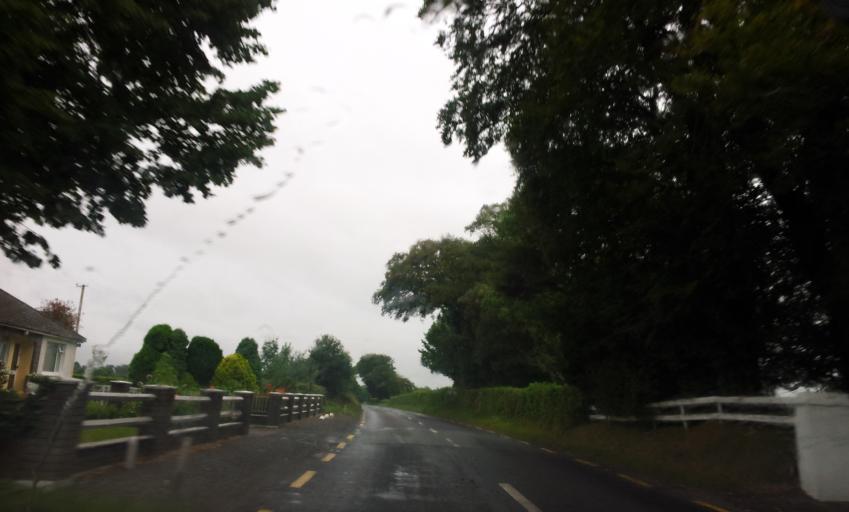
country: IE
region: Munster
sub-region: County Cork
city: Mallow
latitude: 52.1902
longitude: -8.5283
